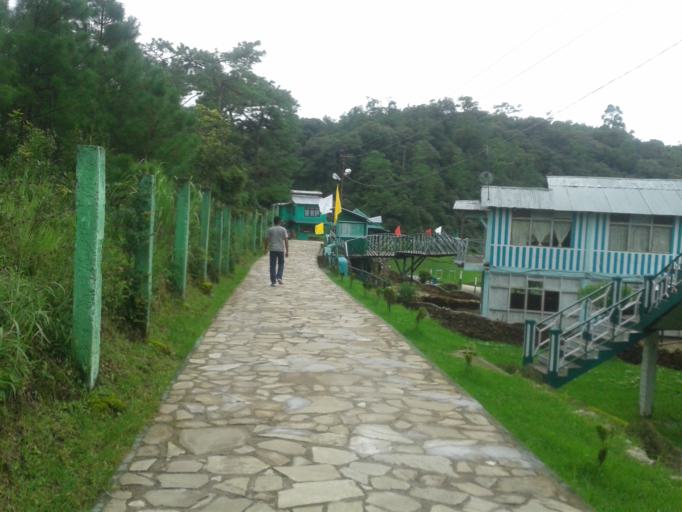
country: IN
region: Meghalaya
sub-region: East Khasi Hills
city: Shillong
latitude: 25.5394
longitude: 91.8218
